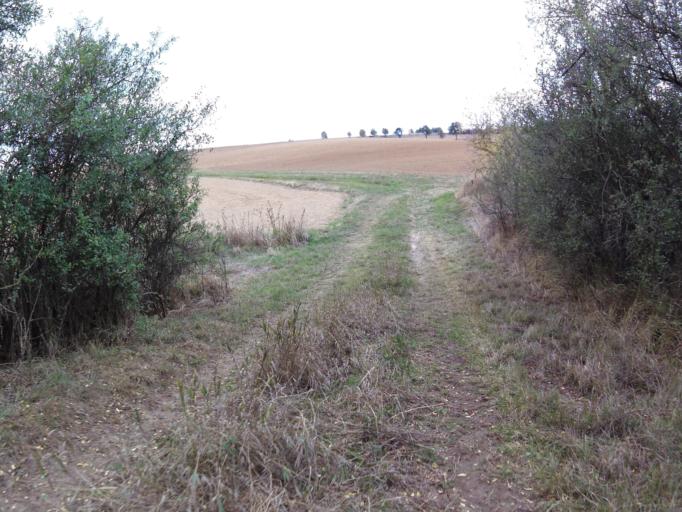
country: DE
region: Bavaria
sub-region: Regierungsbezirk Unterfranken
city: Reichenberg
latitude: 49.7285
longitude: 9.9382
